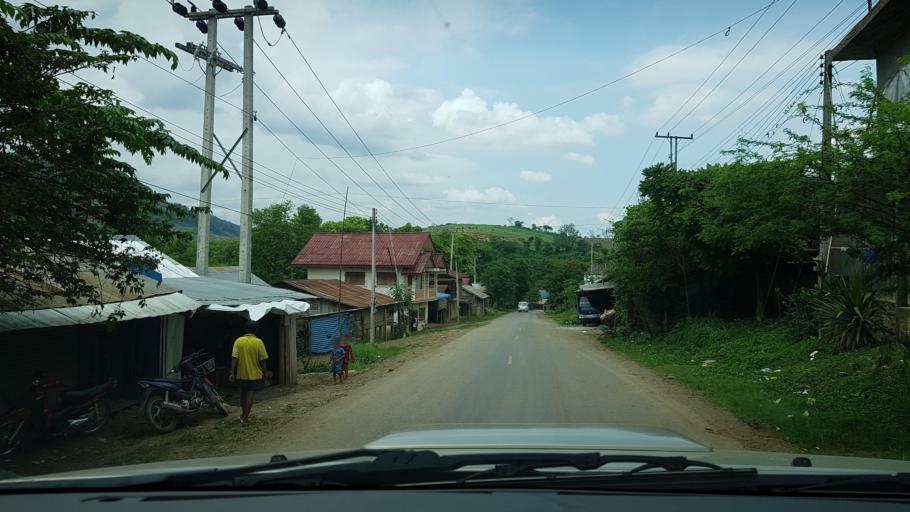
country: TH
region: Nan
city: Chaloem Phra Kiat
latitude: 20.0080
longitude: 101.3046
